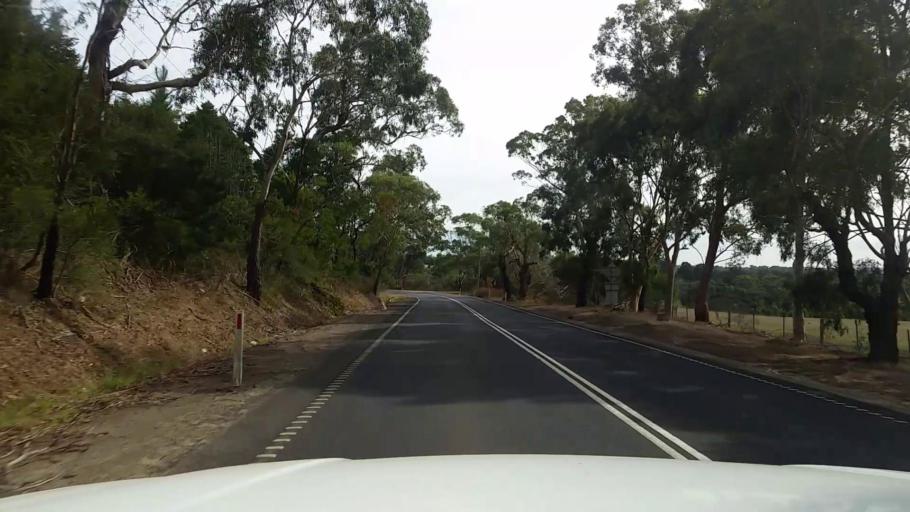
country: AU
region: Victoria
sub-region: Mornington Peninsula
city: Mount Martha
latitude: -38.2860
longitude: 145.0708
